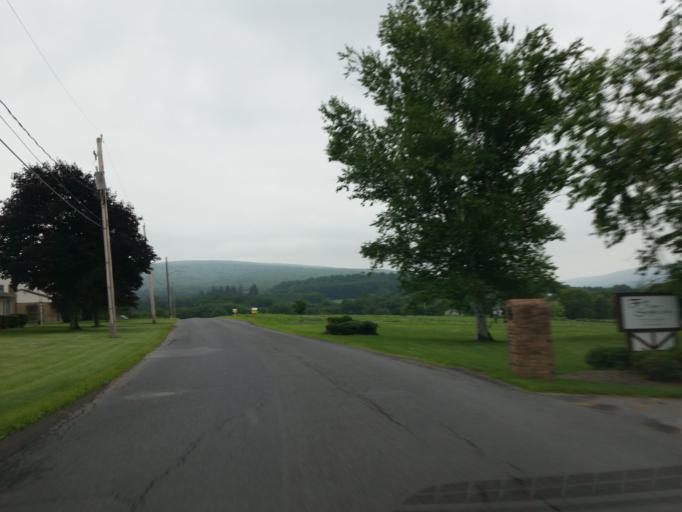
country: US
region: Pennsylvania
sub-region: Schuylkill County
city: Tower City
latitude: 40.5830
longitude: -76.5390
